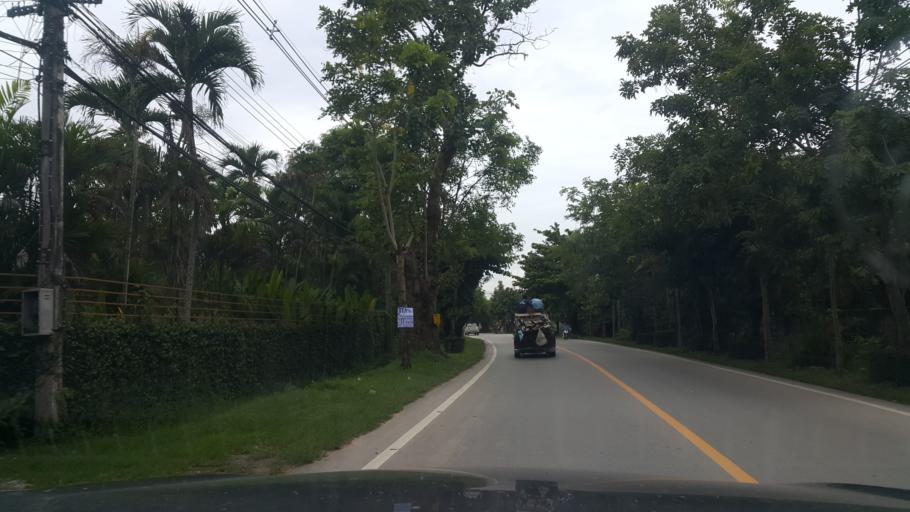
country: TH
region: Chiang Mai
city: San Sai
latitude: 18.8649
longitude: 99.0524
